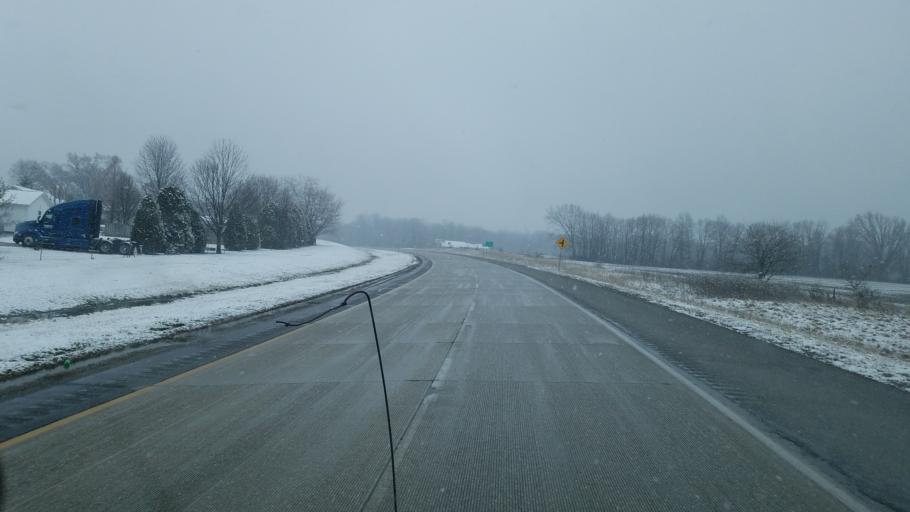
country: US
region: Indiana
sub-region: Grant County
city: Marion
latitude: 40.5524
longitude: -85.6379
